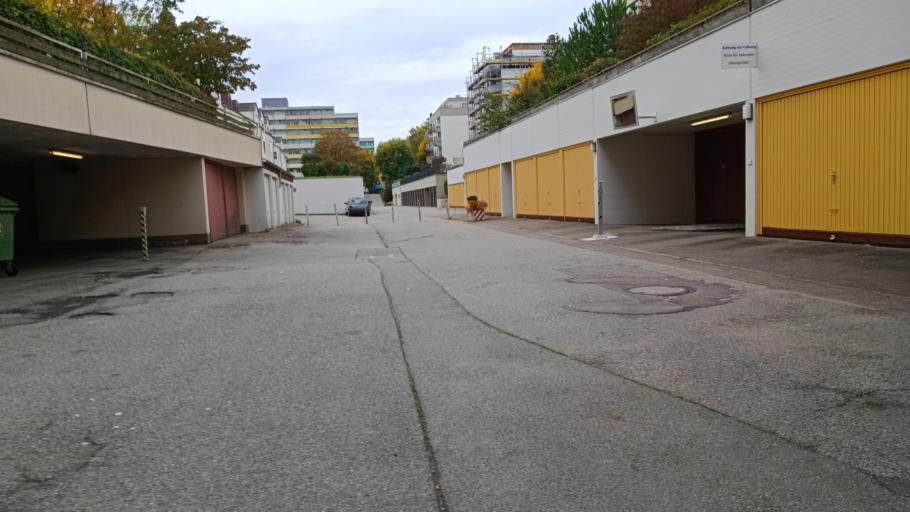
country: DE
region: Bavaria
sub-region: Swabia
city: Augsburg
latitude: 48.3389
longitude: 10.8823
